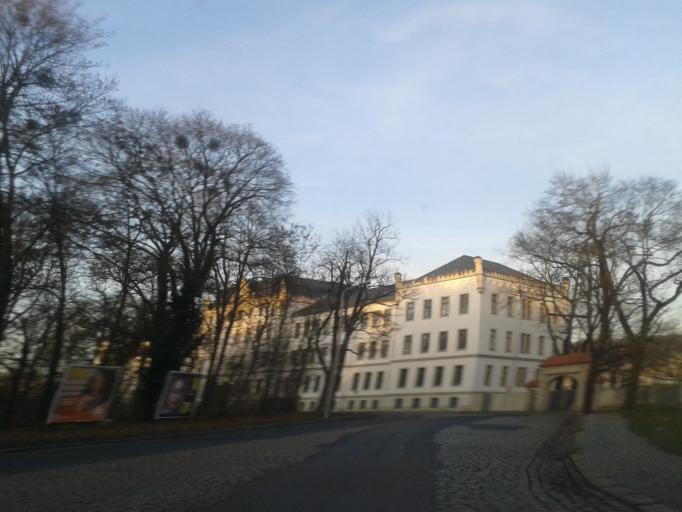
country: DE
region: Saxony
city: Albertstadt
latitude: 51.0869
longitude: 13.7438
